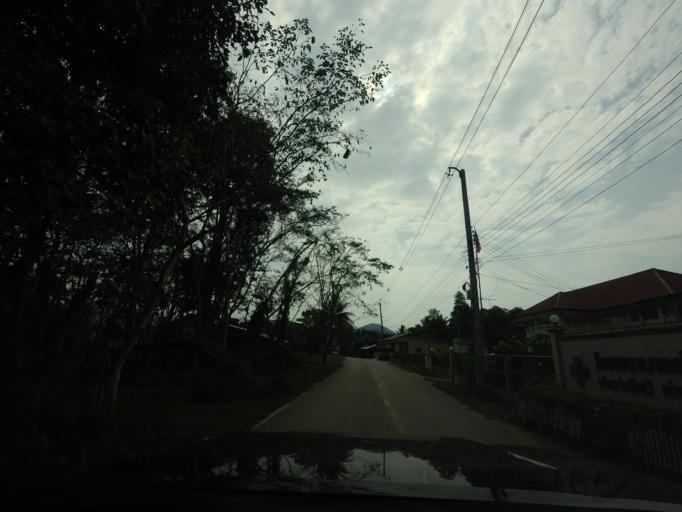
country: TH
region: Loei
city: Chiang Khan
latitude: 17.8116
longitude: 101.5546
